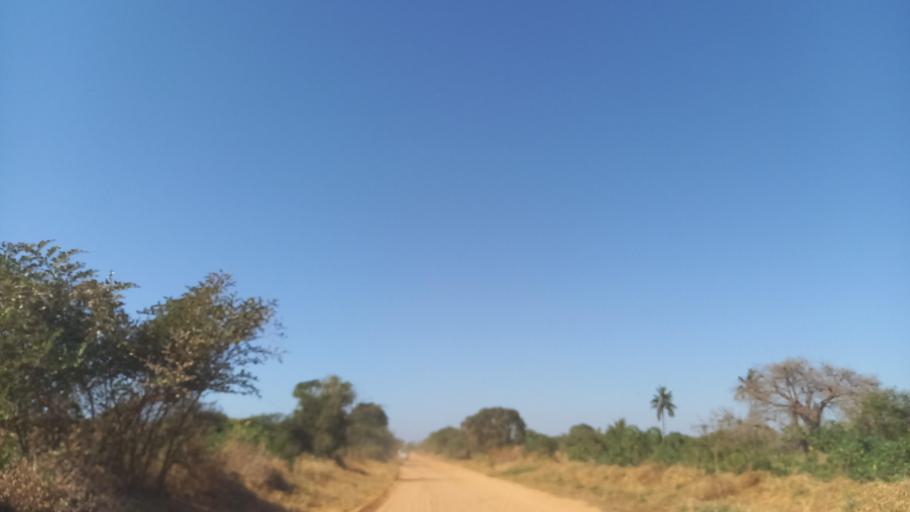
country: MZ
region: Cabo Delgado
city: Pemba
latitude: -13.1564
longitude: 40.5583
